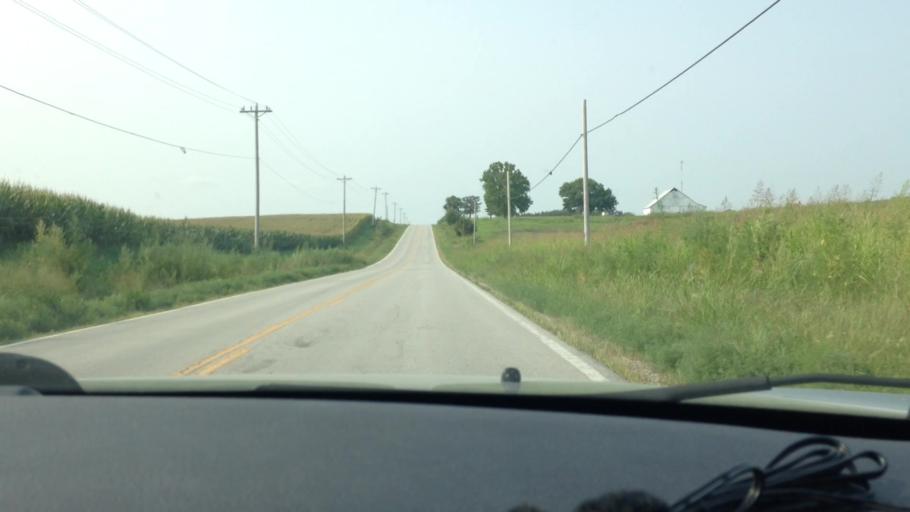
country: US
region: Missouri
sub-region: Platte County
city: Platte City
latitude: 39.4045
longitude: -94.7959
